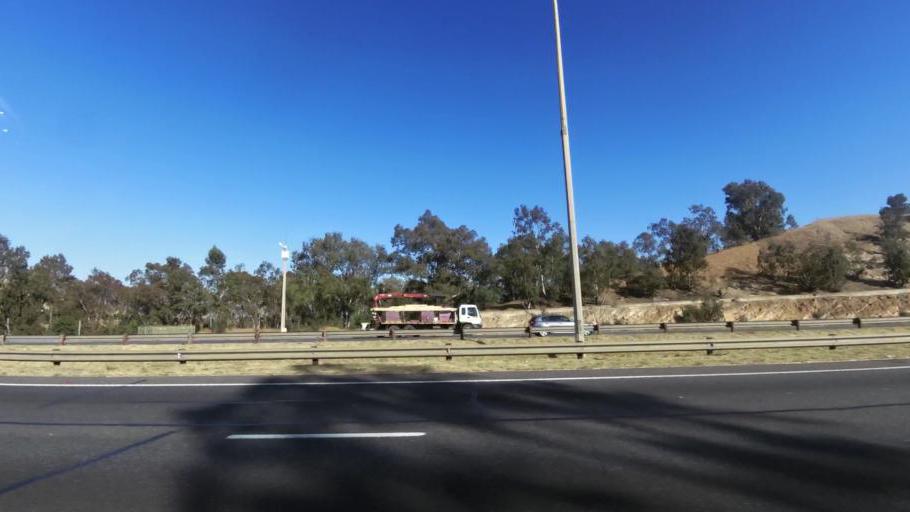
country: ZA
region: Gauteng
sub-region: City of Johannesburg Metropolitan Municipality
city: Johannesburg
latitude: -26.2100
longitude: 27.9576
